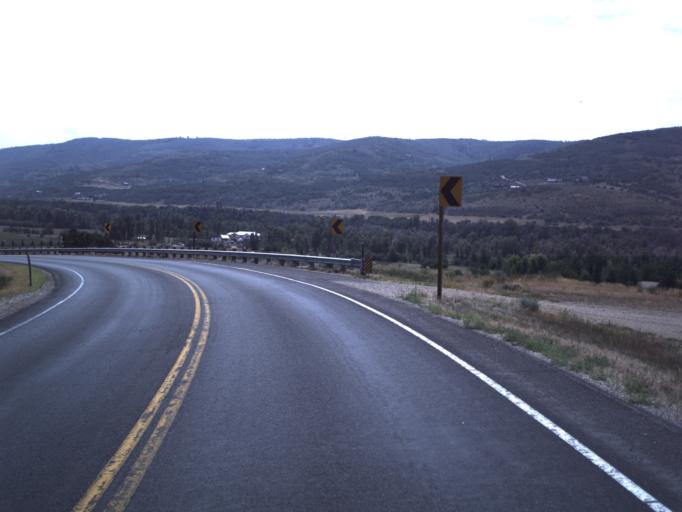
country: US
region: Utah
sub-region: Summit County
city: Francis
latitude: 40.5863
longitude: -111.2422
